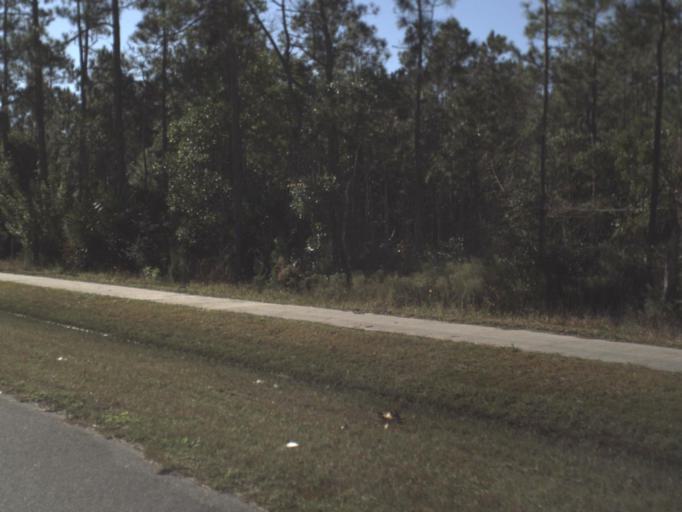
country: US
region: Florida
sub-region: Volusia County
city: Holly Hill
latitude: 29.2352
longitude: -81.0902
